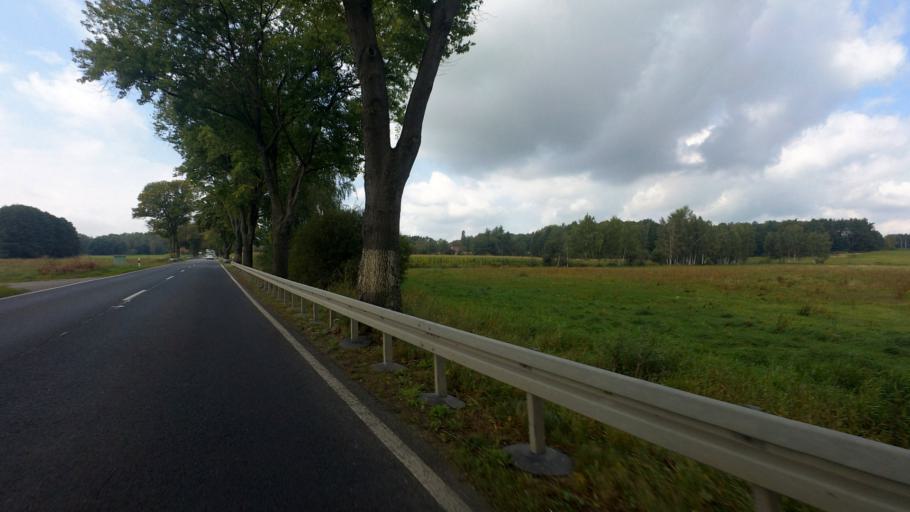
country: DE
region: Brandenburg
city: Hohenleipisch
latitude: 51.4703
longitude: 13.5525
